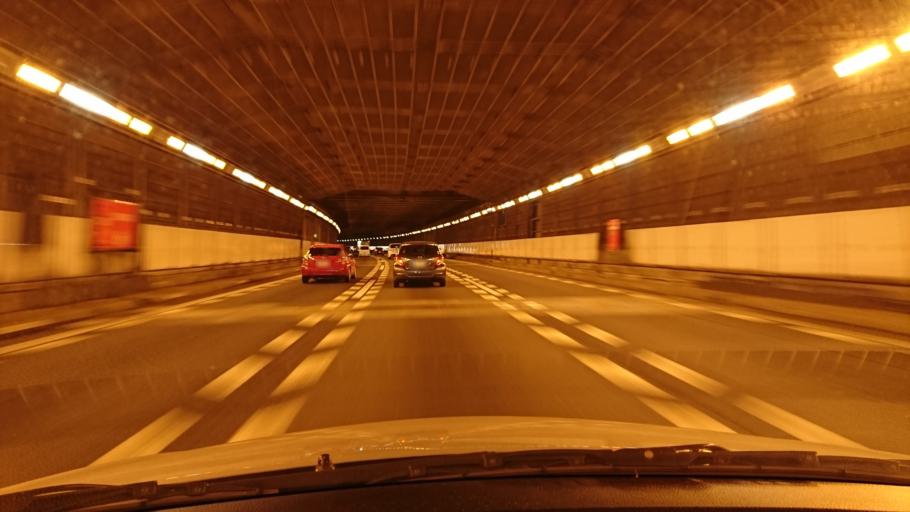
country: JP
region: Hyogo
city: Takarazuka
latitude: 34.8217
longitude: 135.3198
